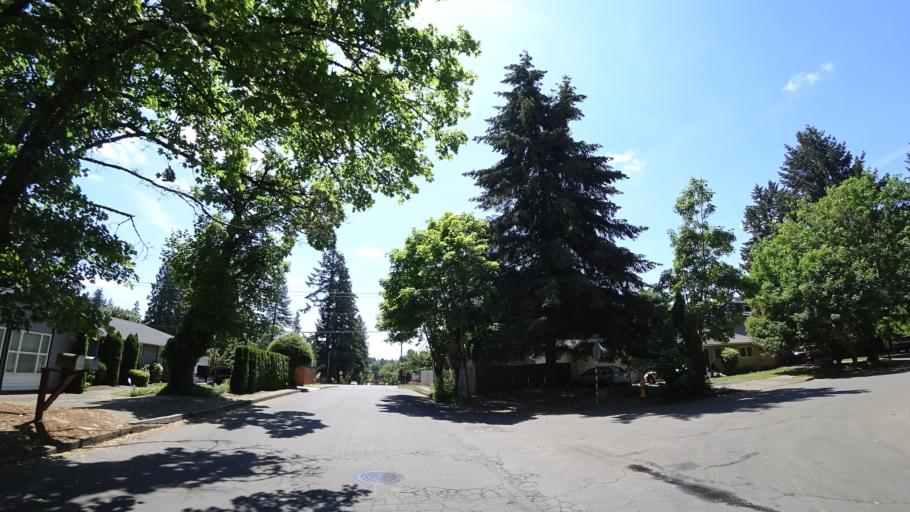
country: US
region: Oregon
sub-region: Washington County
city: Tigard
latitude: 45.4394
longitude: -122.7952
